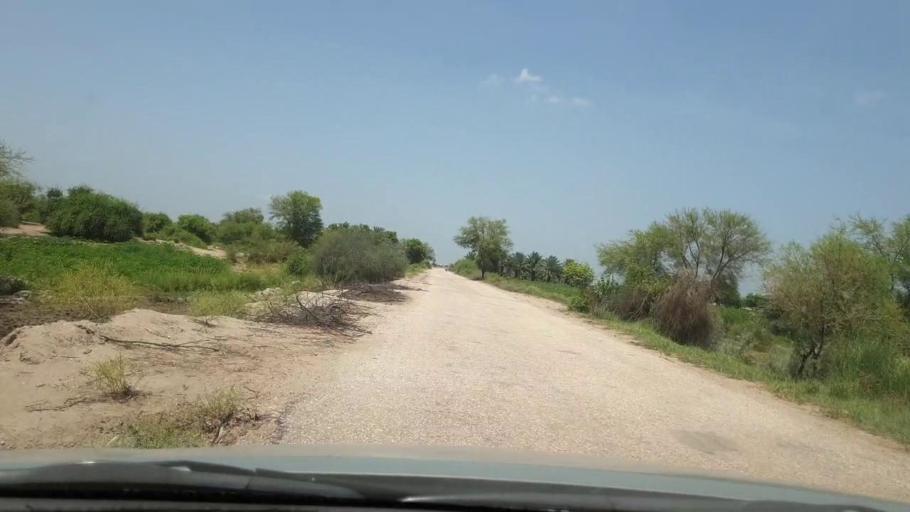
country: PK
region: Sindh
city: Pano Aqil
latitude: 27.7104
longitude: 69.2160
